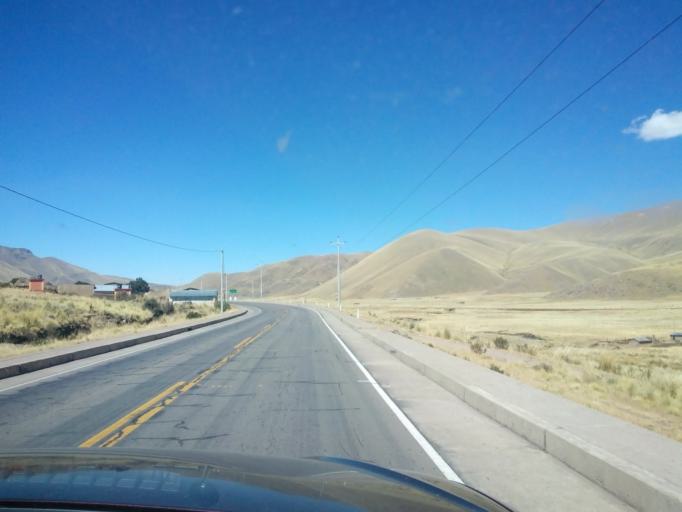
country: PE
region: Puno
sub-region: Provincia de Melgar
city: Santa Rosa
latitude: -14.5125
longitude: -70.9225
